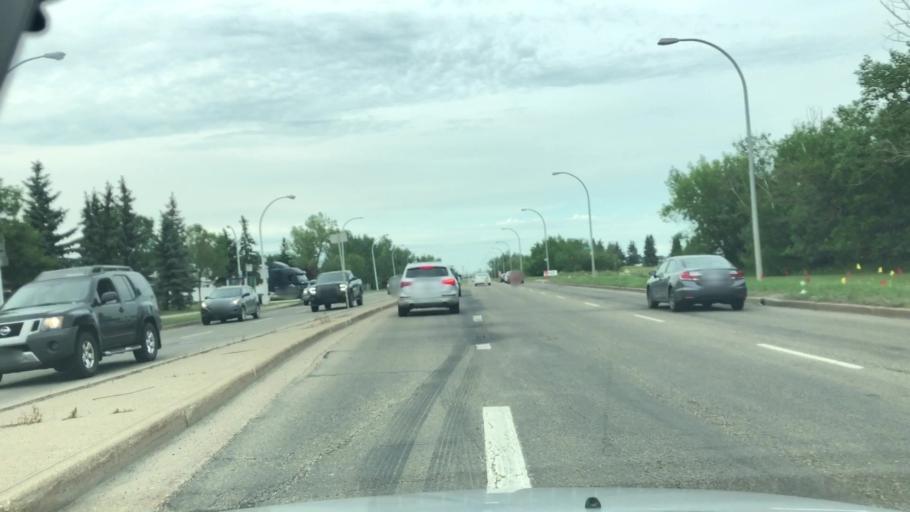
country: CA
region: Alberta
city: Edmonton
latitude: 53.6013
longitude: -113.5166
